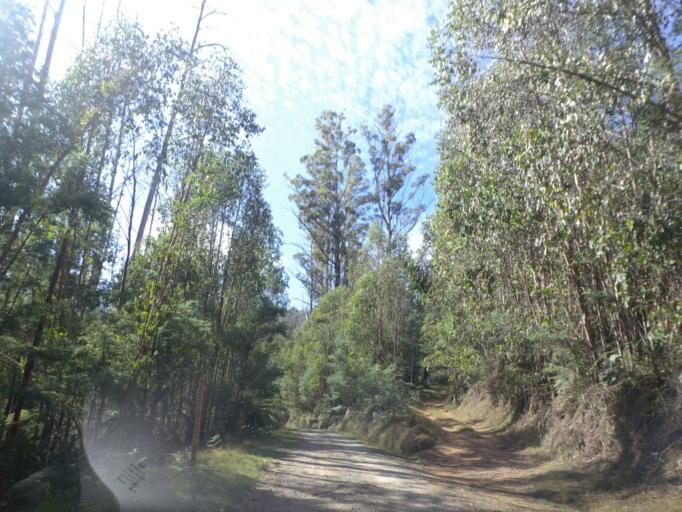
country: AU
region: Victoria
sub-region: Yarra Ranges
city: Millgrove
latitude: -37.5018
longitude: 145.8295
